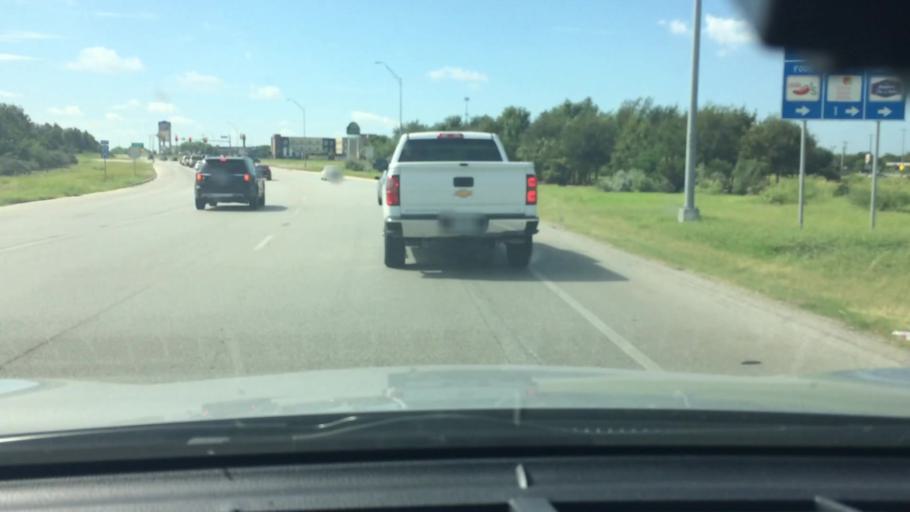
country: US
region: Texas
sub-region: Bexar County
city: China Grove
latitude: 29.3542
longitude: -98.4297
